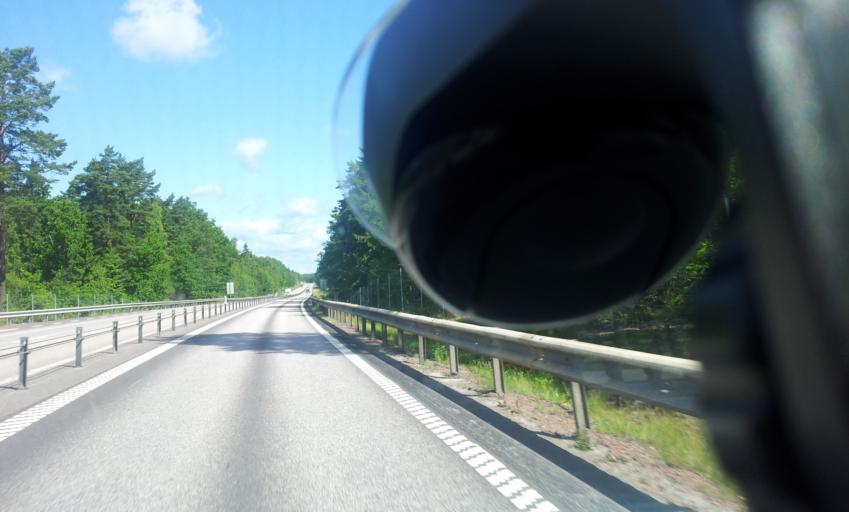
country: SE
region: Kalmar
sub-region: Oskarshamns Kommun
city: Paskallavik
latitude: 57.1665
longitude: 16.4439
